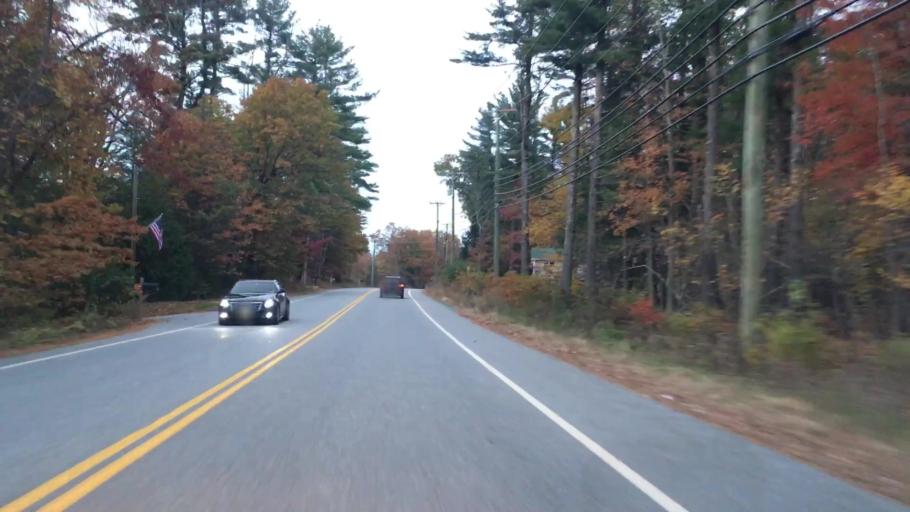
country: US
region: New Hampshire
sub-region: Hillsborough County
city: Milford
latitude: 42.8526
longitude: -71.6355
